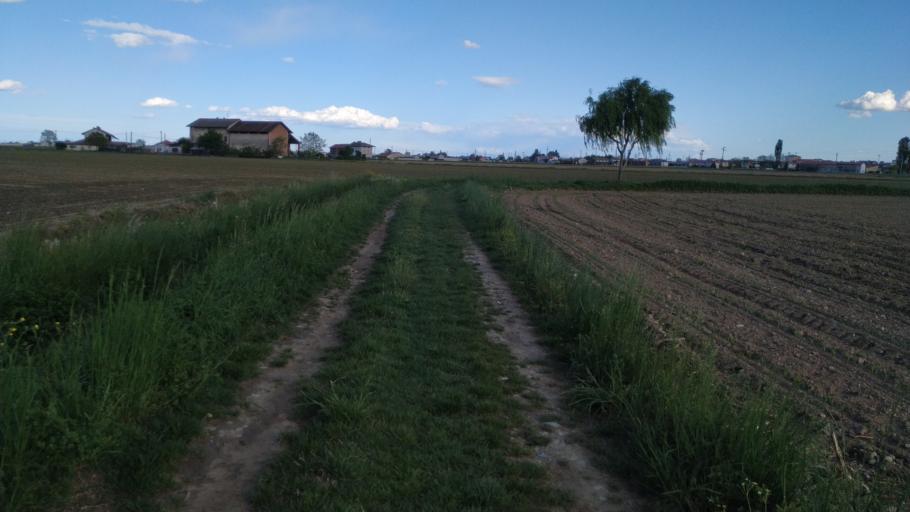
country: IT
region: Piedmont
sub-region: Provincia di Vercelli
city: Santhia
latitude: 45.3806
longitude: 8.1658
